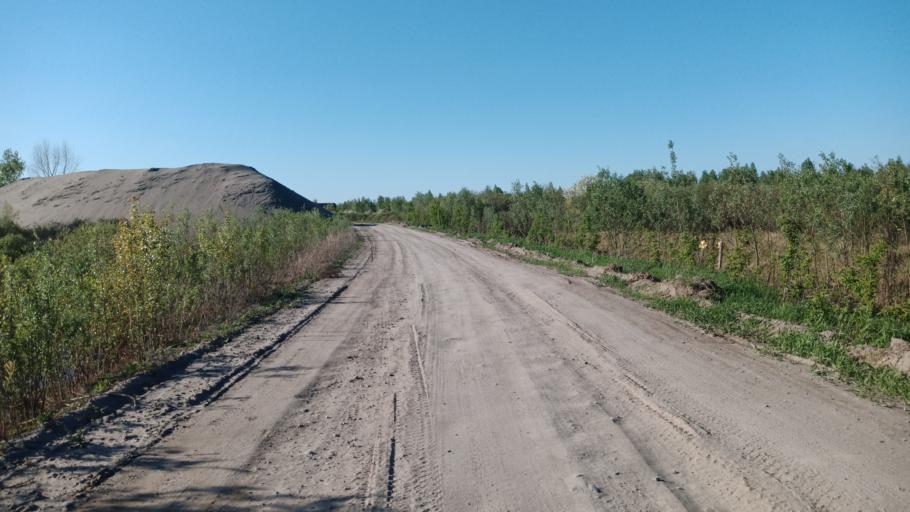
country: RU
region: Altai Krai
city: Zaton
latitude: 53.3086
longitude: 83.8236
